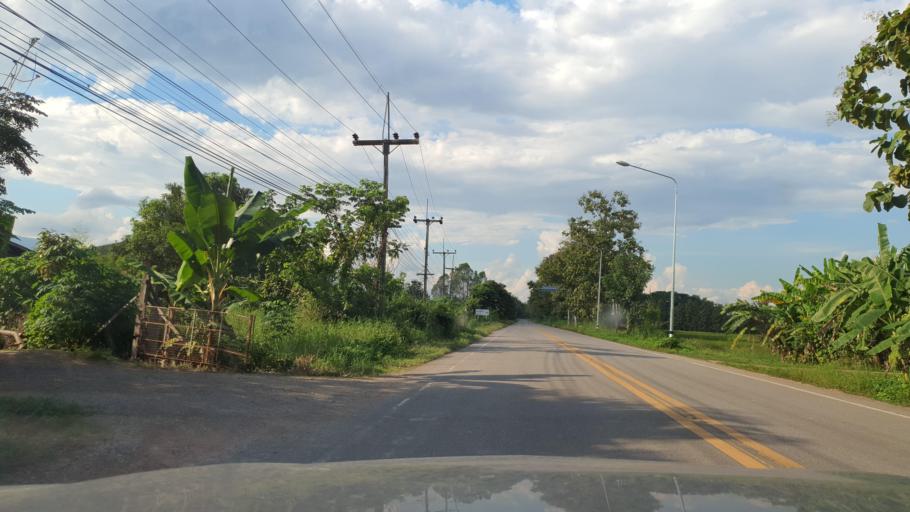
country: TH
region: Phayao
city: Phayao
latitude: 19.1224
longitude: 99.8458
